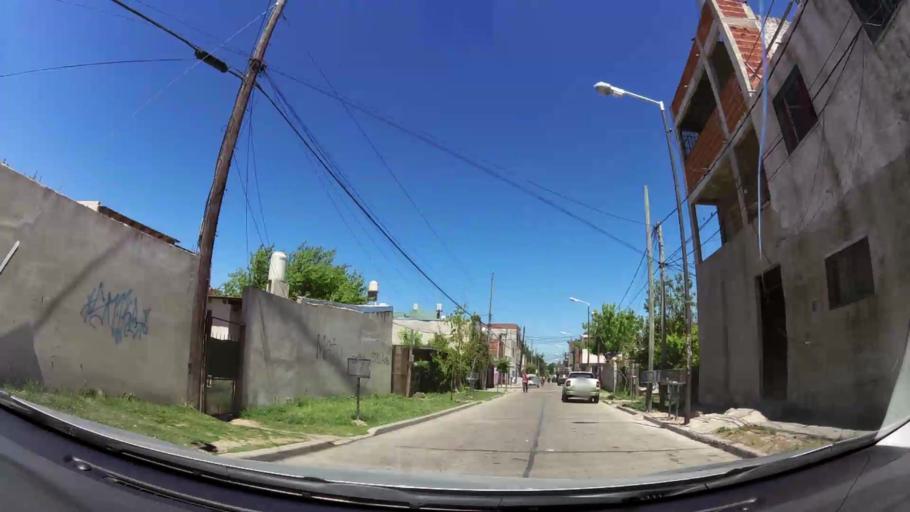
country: AR
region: Buenos Aires
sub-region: Partido de Tigre
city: Tigre
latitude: -34.4597
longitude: -58.5516
